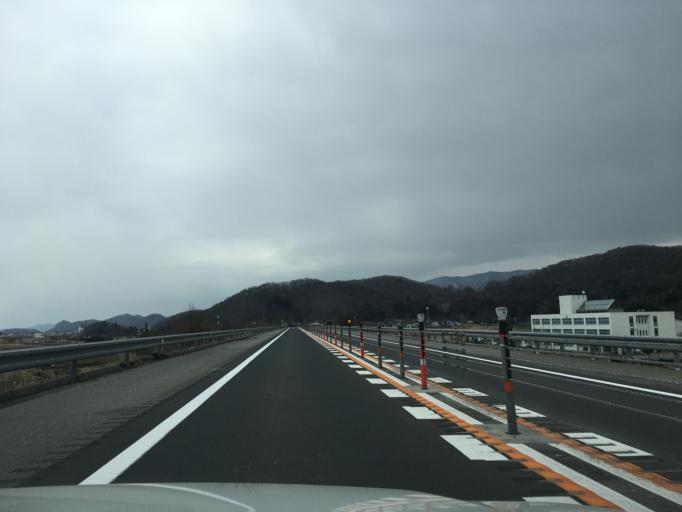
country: JP
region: Aomori
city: Aomori Shi
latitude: 40.8102
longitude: 140.8021
